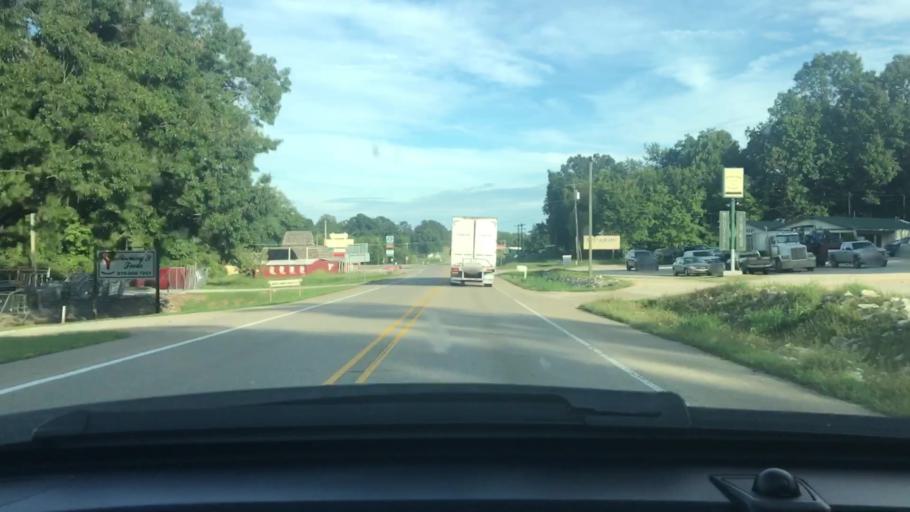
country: US
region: Arkansas
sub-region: Sharp County
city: Cherokee Village
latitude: 36.2374
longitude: -91.2550
